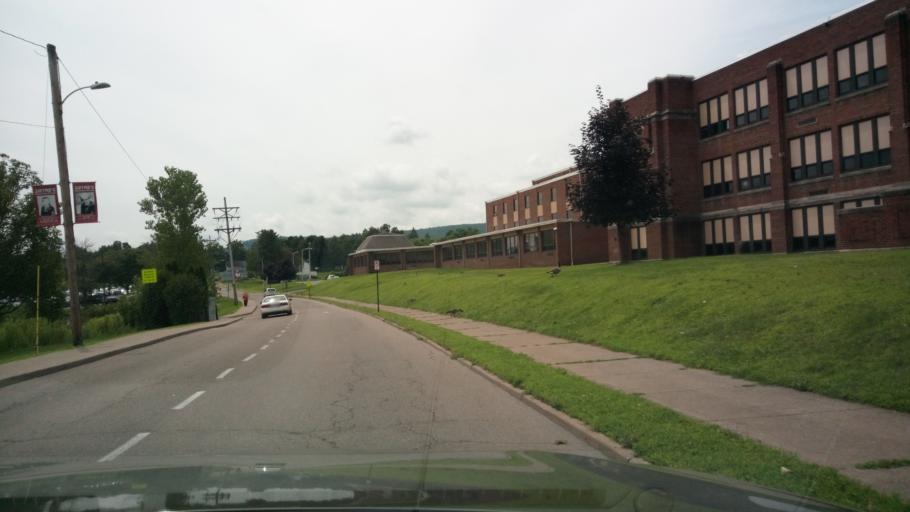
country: US
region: Pennsylvania
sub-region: Bradford County
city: Sayre
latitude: 41.9823
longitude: -76.5225
